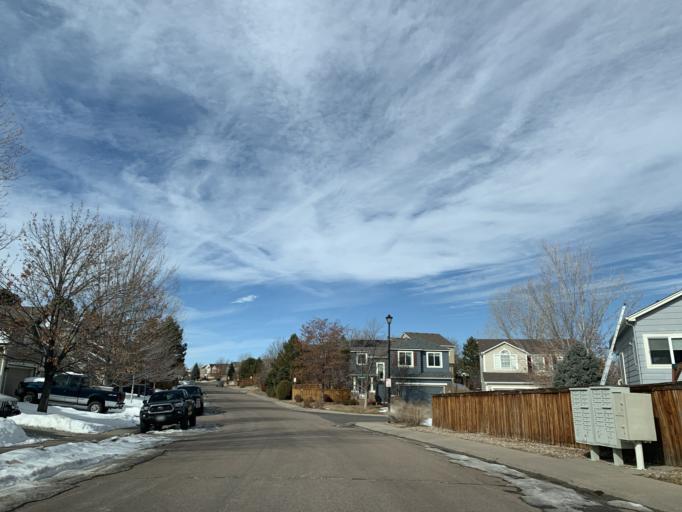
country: US
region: Colorado
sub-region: Douglas County
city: Carriage Club
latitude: 39.5415
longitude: -104.9288
